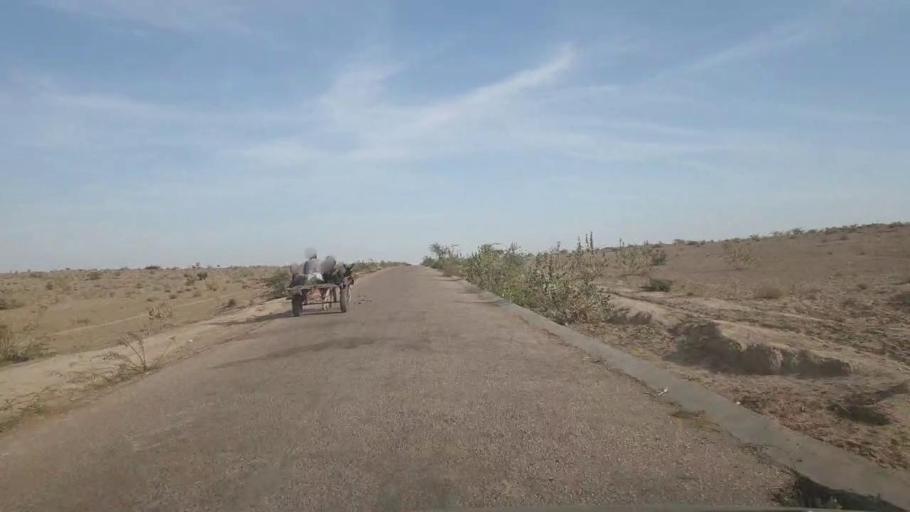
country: PK
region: Sindh
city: Nabisar
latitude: 25.0669
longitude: 69.6496
